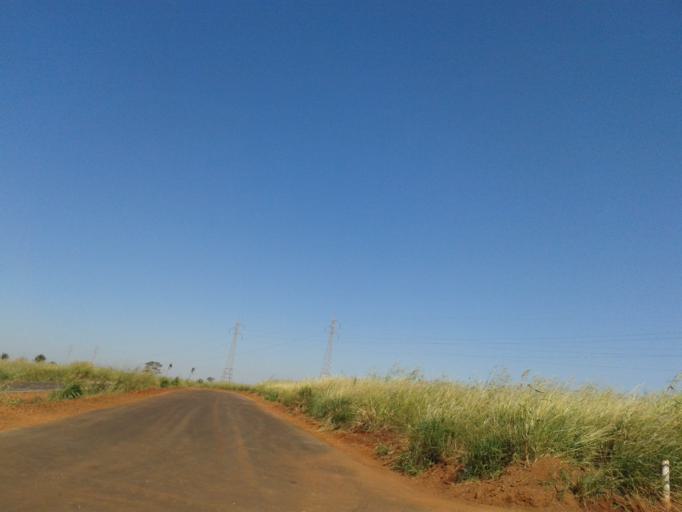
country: BR
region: Minas Gerais
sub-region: Capinopolis
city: Capinopolis
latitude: -18.5362
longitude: -49.5003
